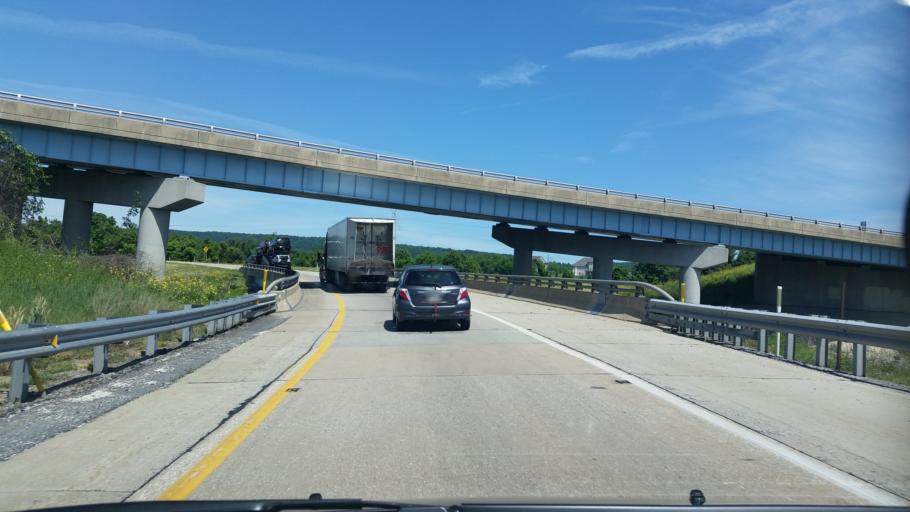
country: US
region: Pennsylvania
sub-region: Cumberland County
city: Mechanicsburg
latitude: 40.2741
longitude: -77.0009
